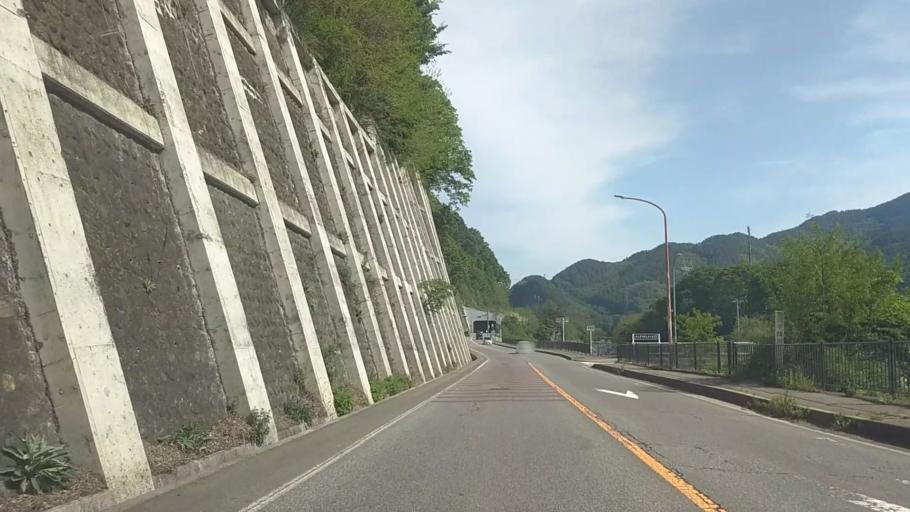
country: JP
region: Nagano
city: Saku
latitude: 36.0994
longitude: 138.4823
